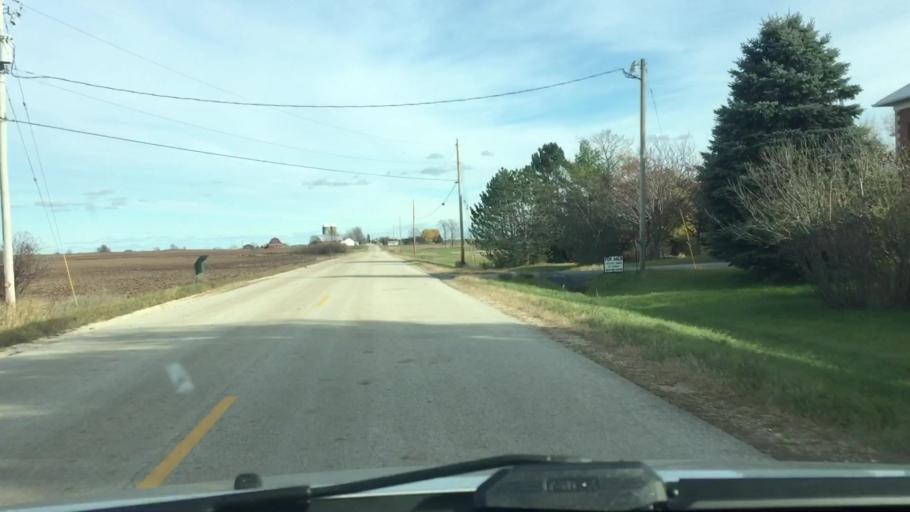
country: US
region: Wisconsin
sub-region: Kewaunee County
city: Luxemburg
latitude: 44.6975
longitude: -87.6101
